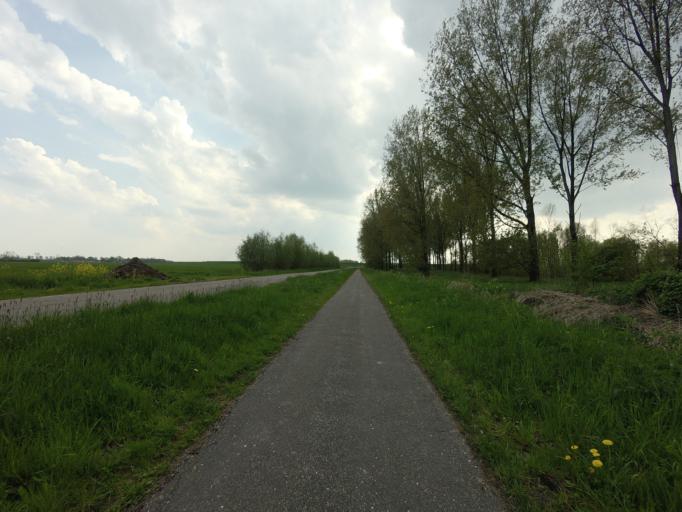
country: NL
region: Utrecht
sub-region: Gemeente Houten
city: Houten
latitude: 51.9952
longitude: 5.1506
